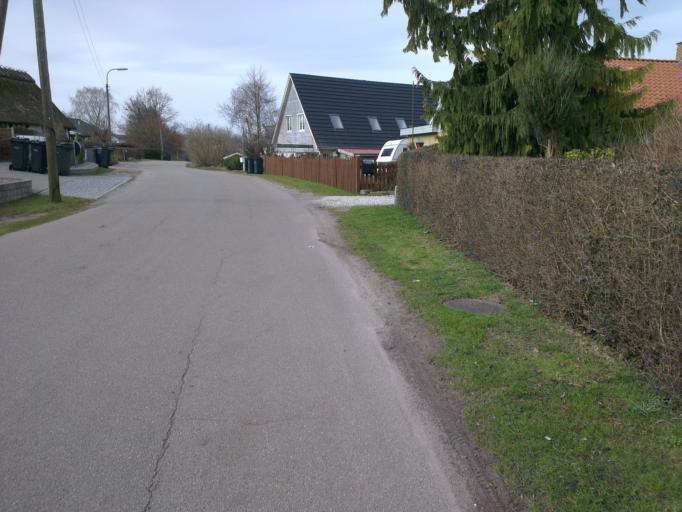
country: DK
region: Capital Region
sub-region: Frederikssund Kommune
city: Frederikssund
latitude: 55.8222
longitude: 12.0208
